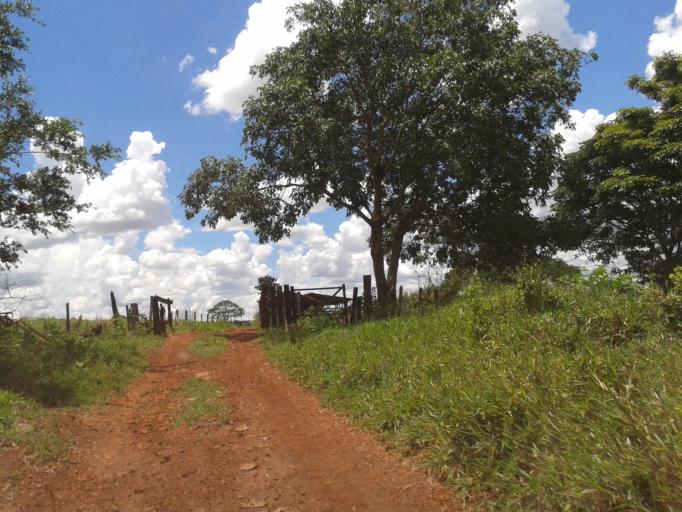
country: BR
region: Minas Gerais
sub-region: Santa Vitoria
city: Santa Vitoria
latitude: -18.7871
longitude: -49.8622
